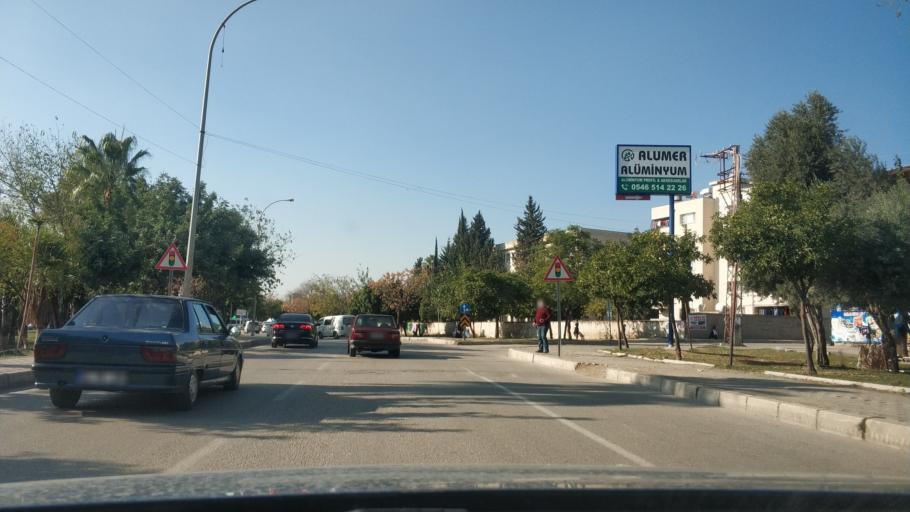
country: TR
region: Adana
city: Seyhan
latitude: 37.0122
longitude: 35.2826
